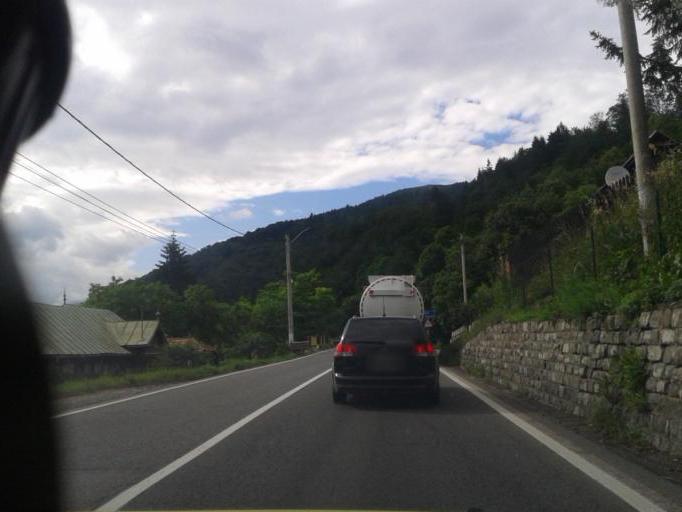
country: RO
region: Prahova
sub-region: Comuna Comarnic
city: Posada
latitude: 45.2870
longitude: 25.6174
